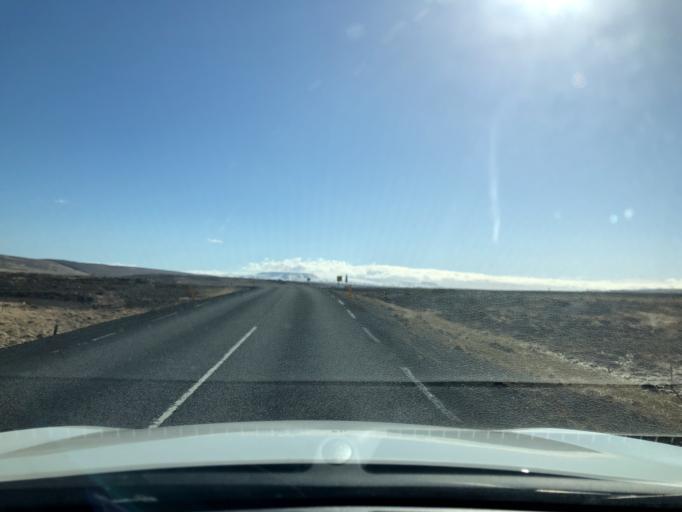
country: IS
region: West
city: Borgarnes
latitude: 64.6196
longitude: -21.4849
